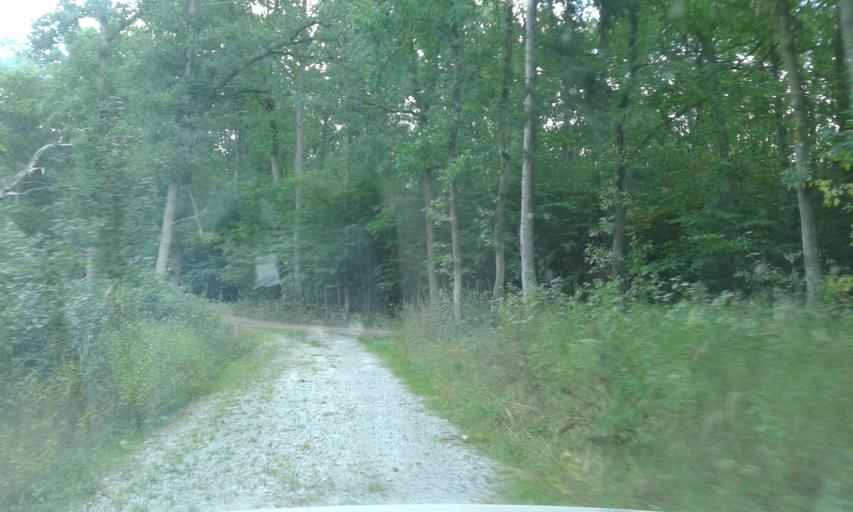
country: PL
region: West Pomeranian Voivodeship
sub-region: Powiat stargardzki
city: Dolice
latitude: 53.2293
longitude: 15.2605
